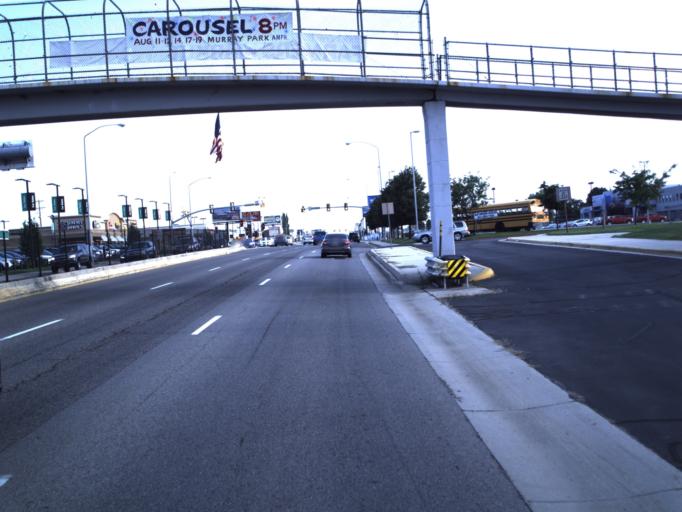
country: US
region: Utah
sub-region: Salt Lake County
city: Murray
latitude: 40.6538
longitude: -111.8885
